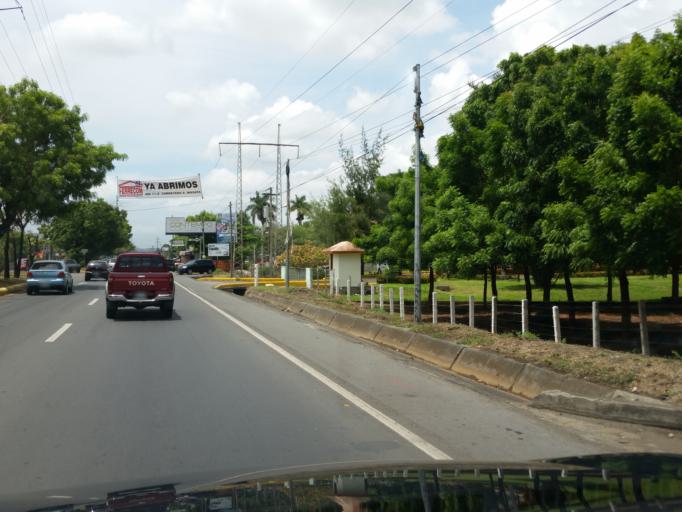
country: NI
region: Masaya
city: Ticuantepe
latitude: 12.0787
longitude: -86.2240
